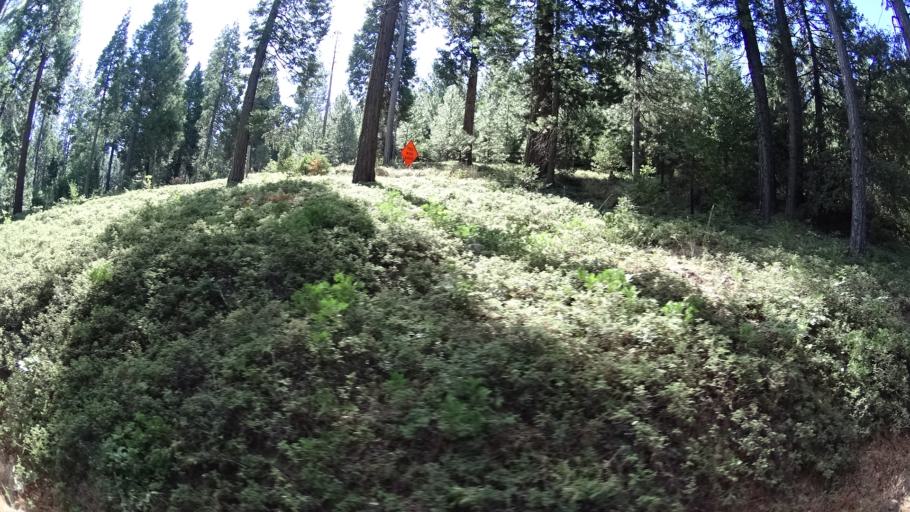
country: US
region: California
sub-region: Amador County
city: Pioneer
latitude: 38.3964
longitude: -120.4408
